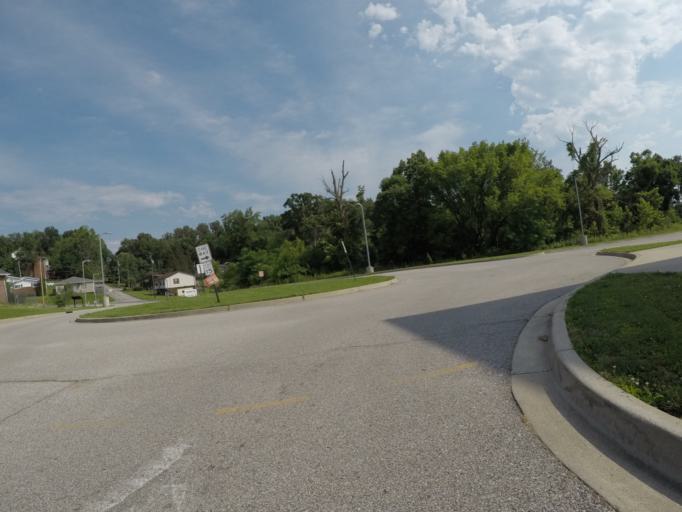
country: US
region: West Virginia
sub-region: Cabell County
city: Pea Ridge
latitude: 38.4093
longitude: -82.3715
